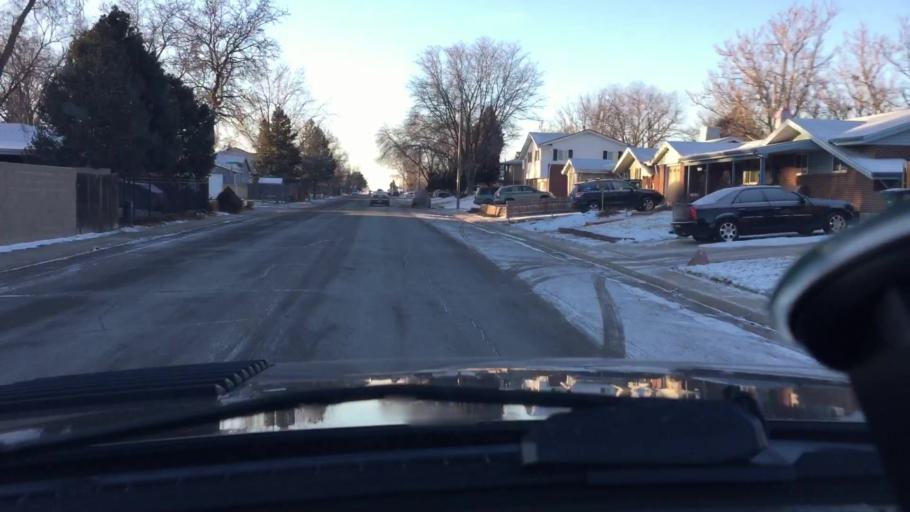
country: US
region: Colorado
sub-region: Adams County
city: Northglenn
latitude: 39.8814
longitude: -105.0056
